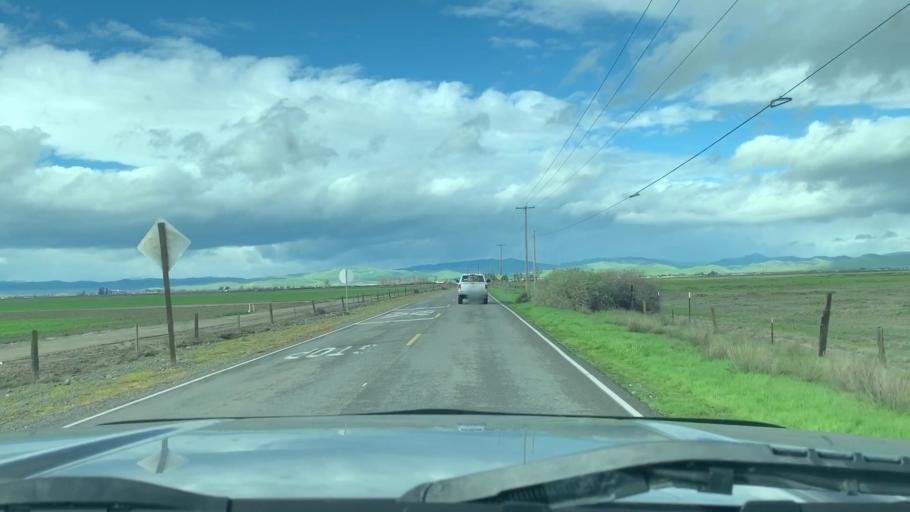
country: US
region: California
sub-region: Merced County
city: Los Banos
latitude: 37.1237
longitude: -120.9463
